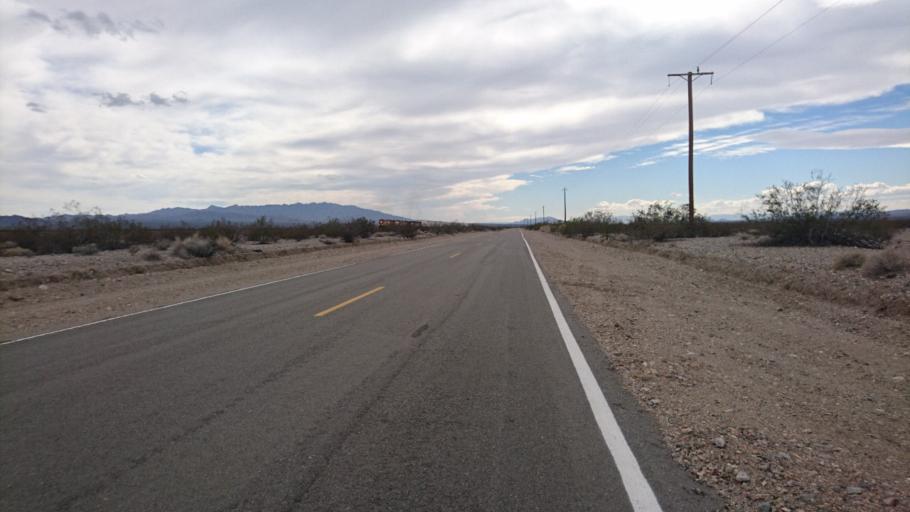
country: US
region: California
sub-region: San Bernardino County
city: Needles
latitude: 34.7831
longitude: -115.2057
